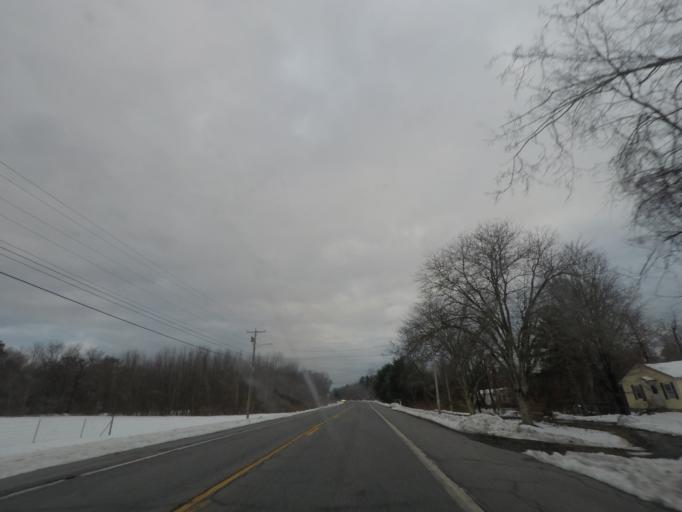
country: US
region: New York
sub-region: Ulster County
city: Plattekill
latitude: 41.6512
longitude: -74.1123
